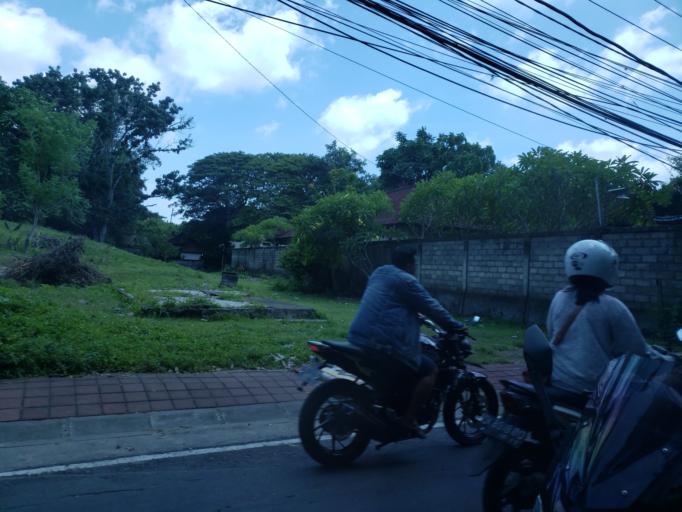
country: ID
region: Bali
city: Jimbaran
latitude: -8.7803
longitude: 115.1679
